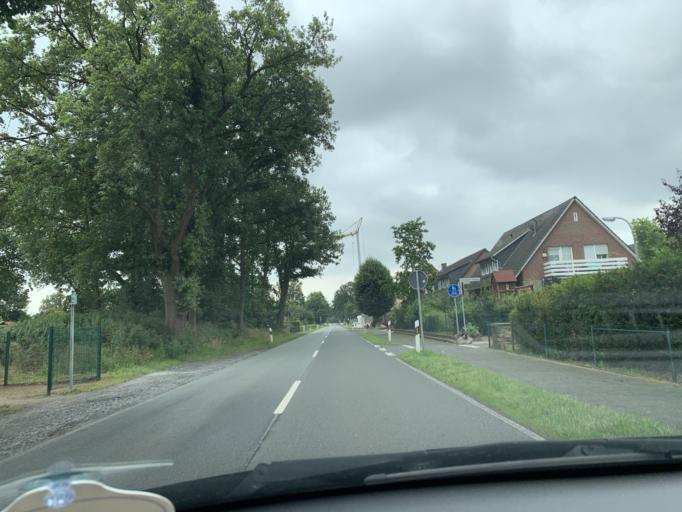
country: DE
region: North Rhine-Westphalia
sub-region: Regierungsbezirk Munster
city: Ostbevern
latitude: 52.0556
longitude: 7.8430
